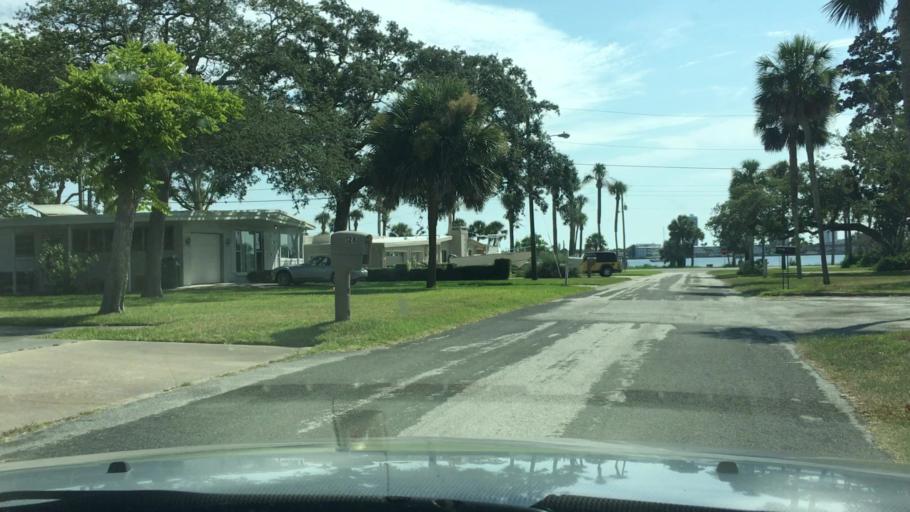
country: US
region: Florida
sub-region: Volusia County
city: Holly Hill
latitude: 29.2611
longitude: -81.0446
